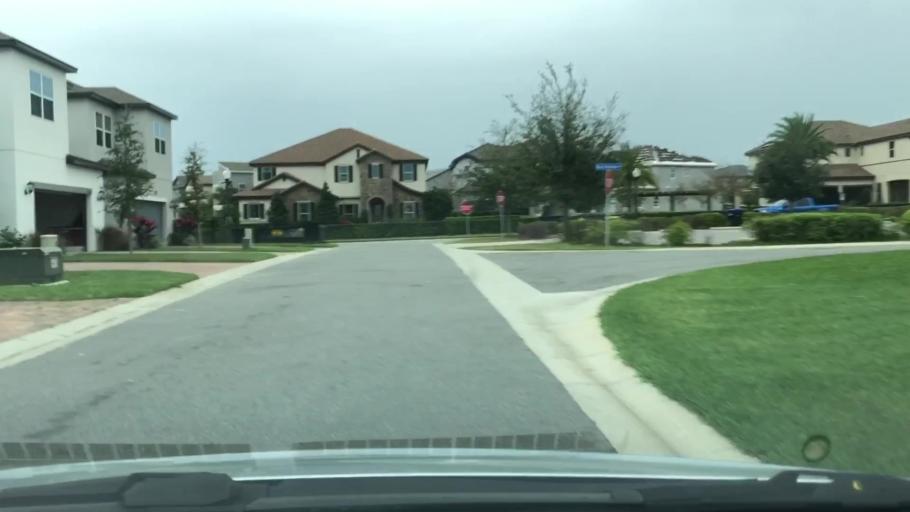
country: US
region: Florida
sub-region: Polk County
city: Citrus Ridge
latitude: 28.4307
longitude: -81.6215
